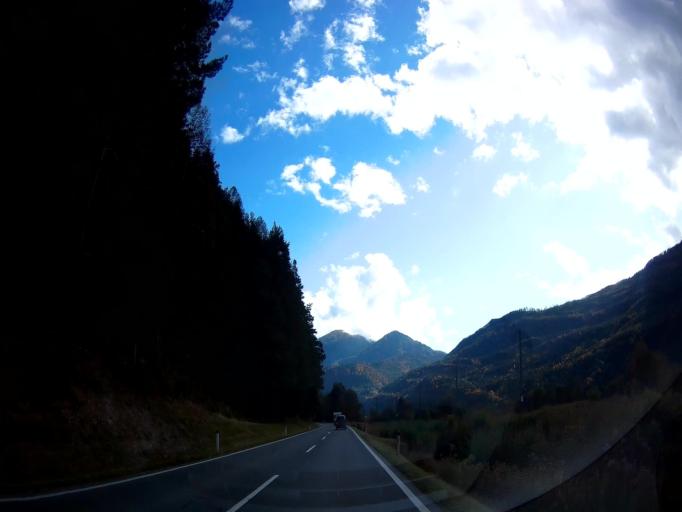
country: AT
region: Carinthia
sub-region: Politischer Bezirk Spittal an der Drau
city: Oberdrauburg
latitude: 46.7595
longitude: 12.9407
